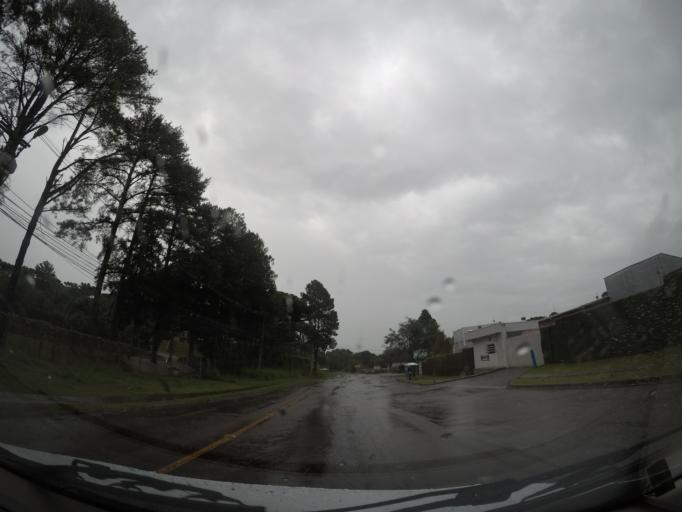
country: BR
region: Parana
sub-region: Curitiba
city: Curitiba
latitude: -25.4531
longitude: -49.3676
